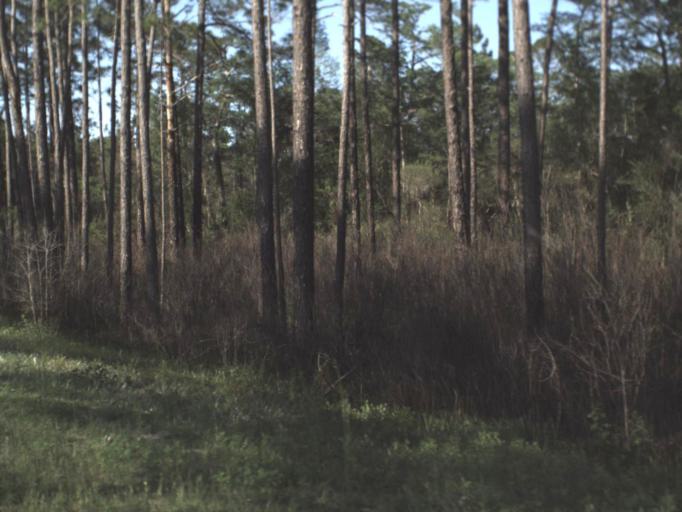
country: US
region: Florida
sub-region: Gulf County
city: Wewahitchka
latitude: 30.0360
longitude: -84.9836
